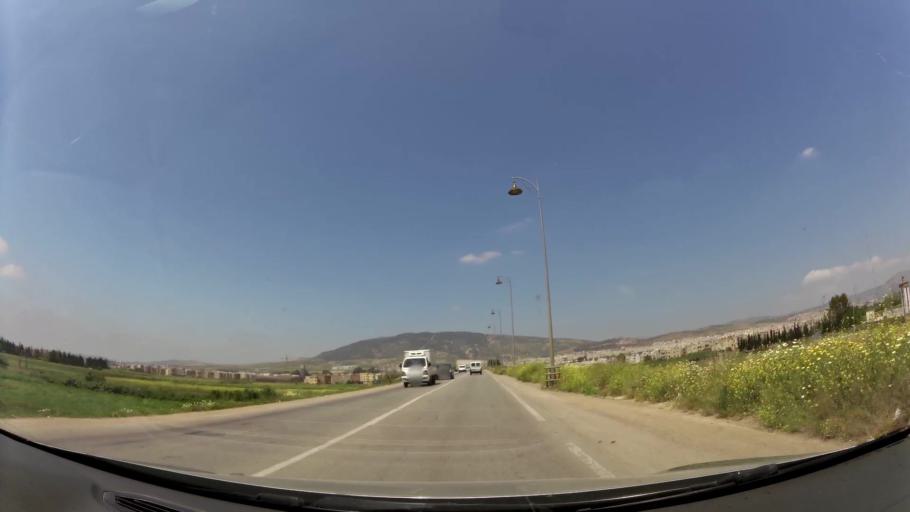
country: MA
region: Fes-Boulemane
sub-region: Fes
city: Fes
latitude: 34.0312
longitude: -5.0296
